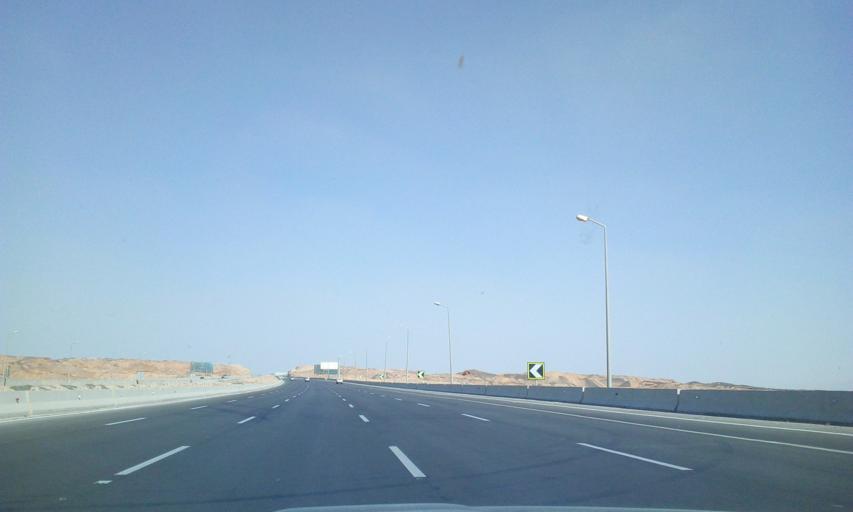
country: EG
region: As Suways
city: Ain Sukhna
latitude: 29.6941
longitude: 32.1183
